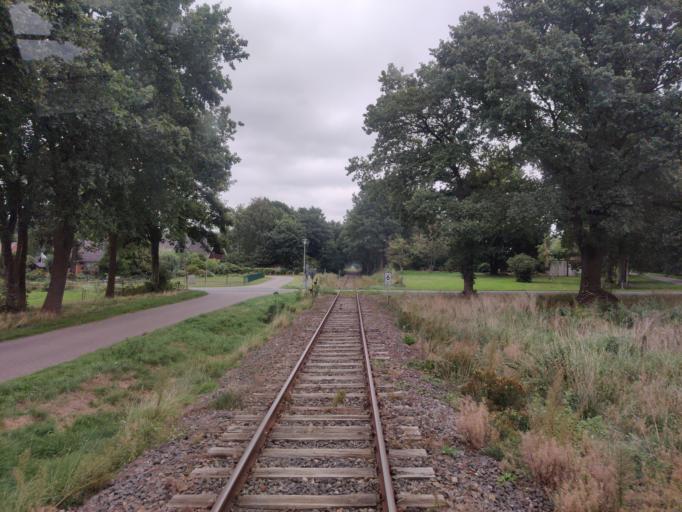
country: DE
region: Lower Saxony
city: Oerel
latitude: 53.4780
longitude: 9.0633
